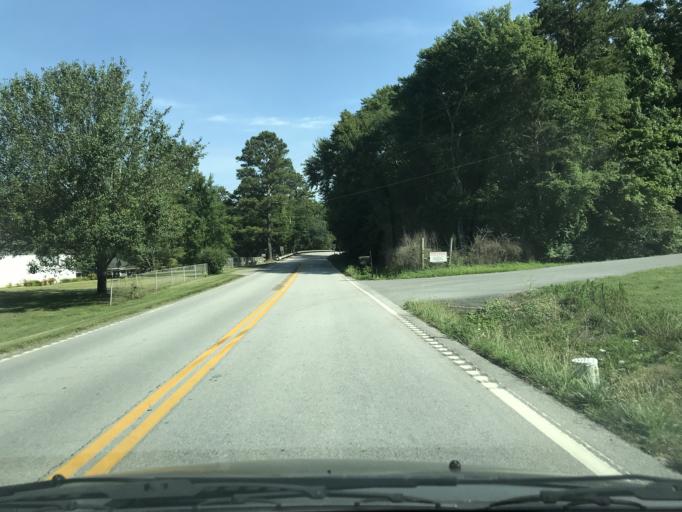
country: US
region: Tennessee
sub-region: Hamilton County
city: Lakesite
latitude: 35.1950
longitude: -85.0701
